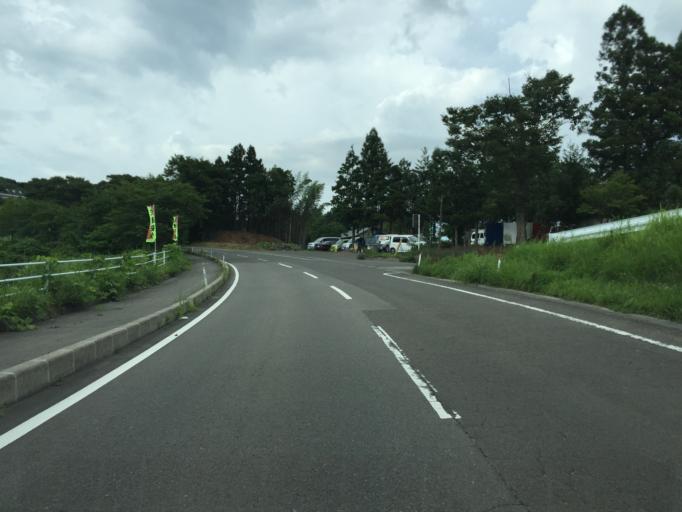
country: JP
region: Fukushima
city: Fukushima-shi
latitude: 37.6838
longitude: 140.5367
